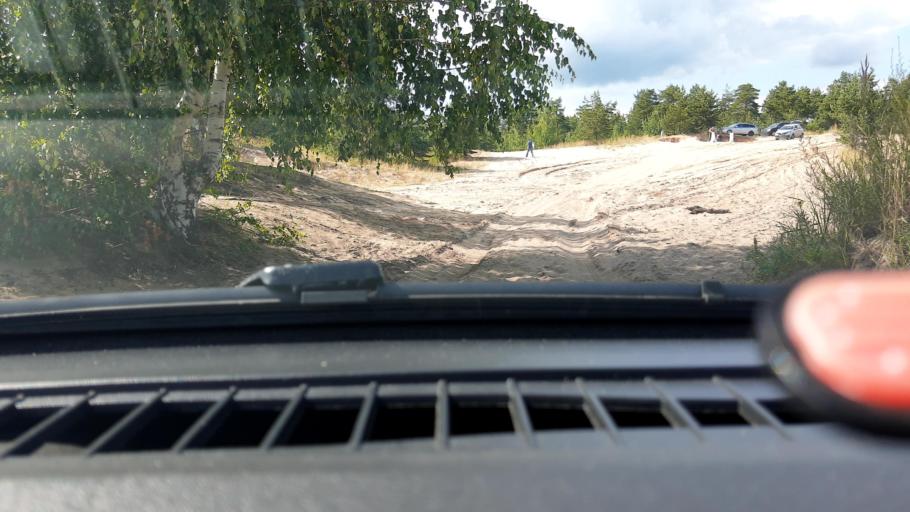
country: RU
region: Nizjnij Novgorod
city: Gorbatovka
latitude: 56.3789
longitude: 43.7665
